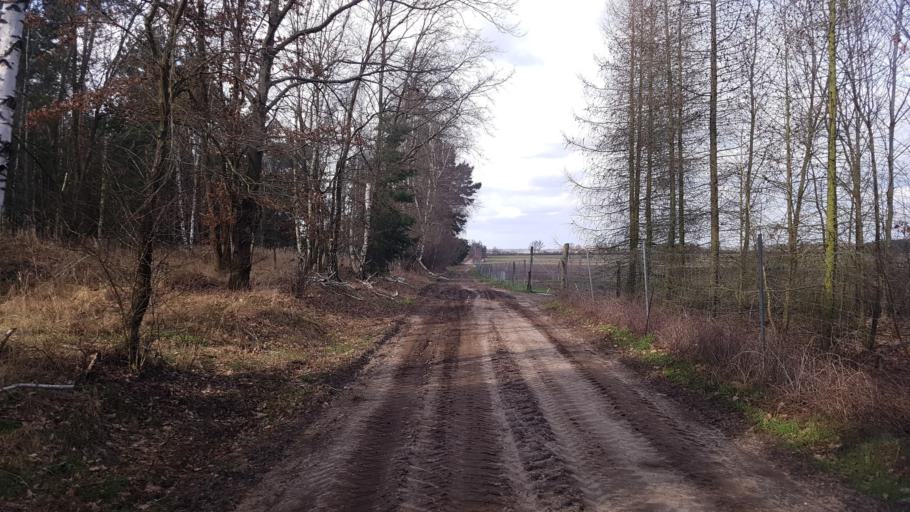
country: DE
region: Brandenburg
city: Herzberg
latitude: 51.6869
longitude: 13.2985
